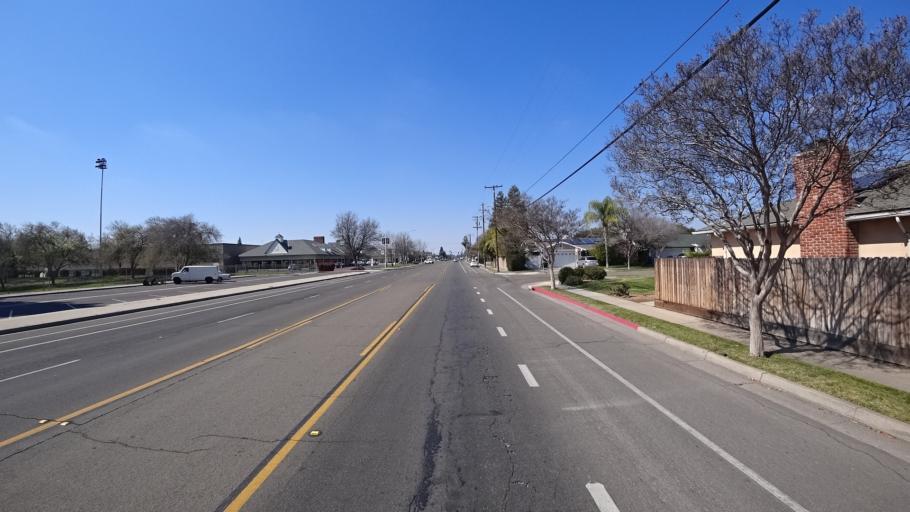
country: US
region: California
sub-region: Fresno County
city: Fresno
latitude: 36.8014
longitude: -119.7692
